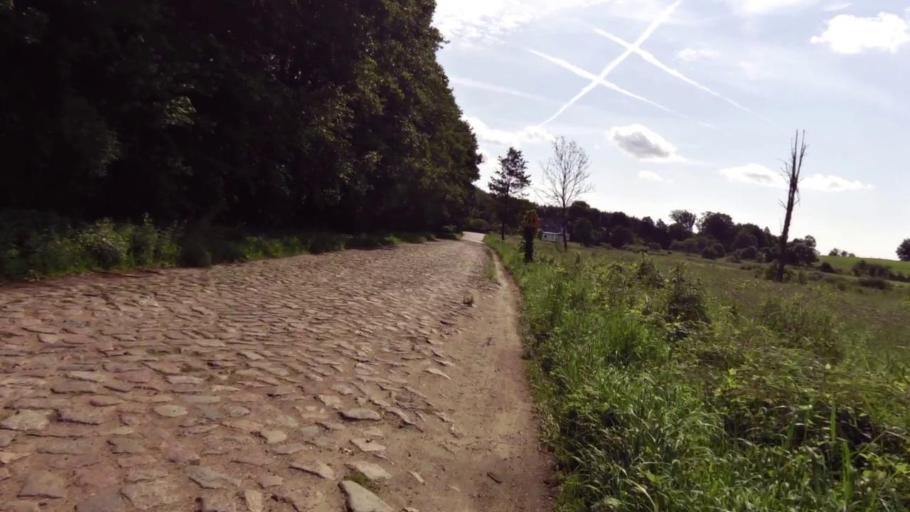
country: PL
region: West Pomeranian Voivodeship
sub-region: Powiat stargardzki
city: Dobrzany
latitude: 53.3898
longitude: 15.4885
